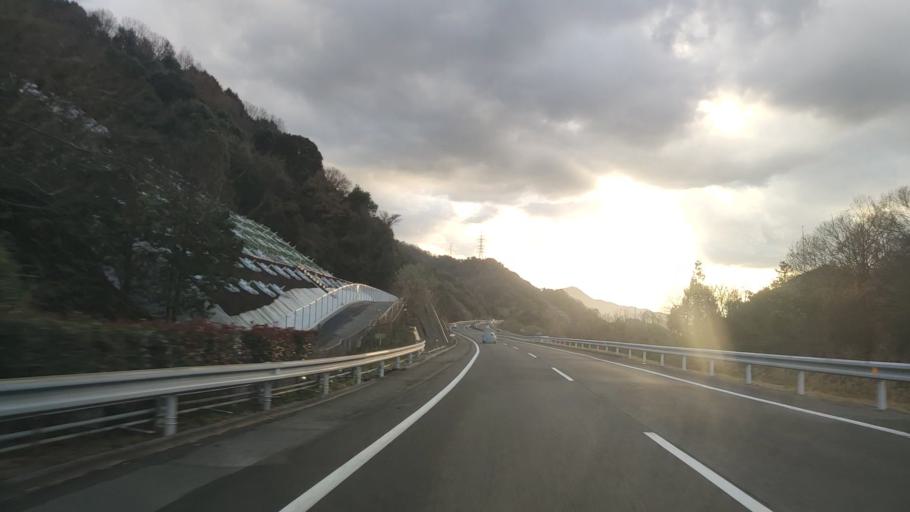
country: JP
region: Ehime
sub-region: Shikoku-chuo Shi
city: Matsuyama
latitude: 33.8166
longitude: 132.9583
